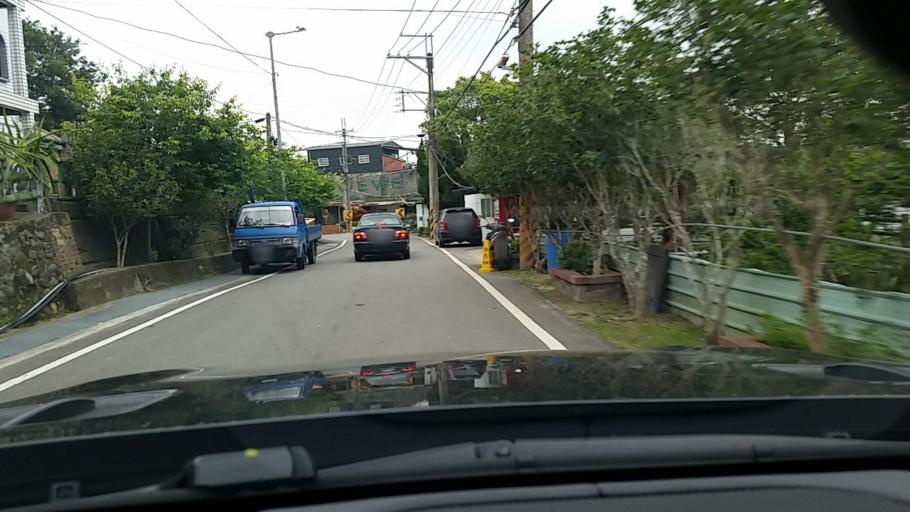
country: TW
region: Taiwan
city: Daxi
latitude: 24.8006
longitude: 121.3061
